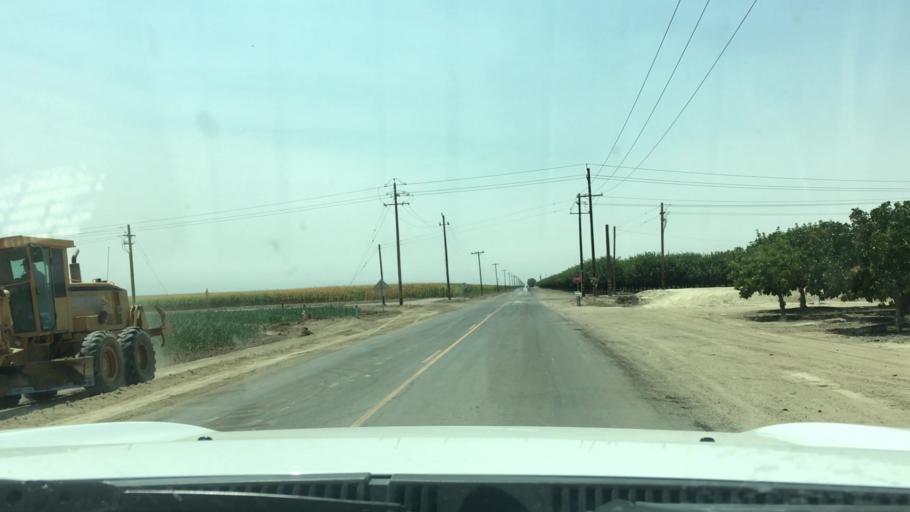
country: US
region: California
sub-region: Kern County
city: Wasco
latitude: 35.7184
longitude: -119.4372
